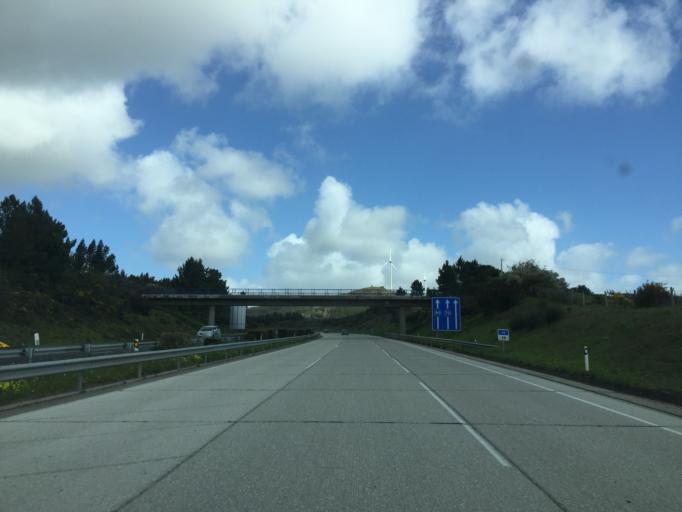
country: PT
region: Lisbon
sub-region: Mafra
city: Milharado
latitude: 39.0072
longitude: -9.2126
